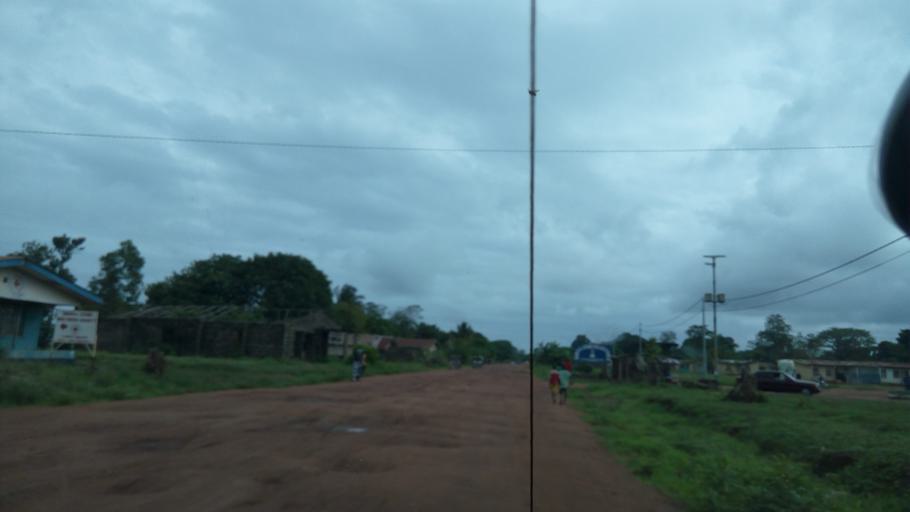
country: SL
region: Northern Province
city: Tintafor
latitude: 8.6231
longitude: -13.2140
